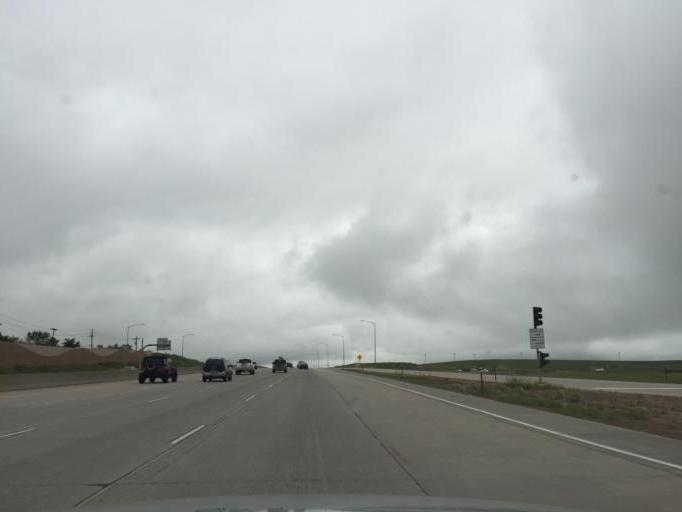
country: US
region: Colorado
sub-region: Park County
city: Castle Pines North
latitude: 39.4737
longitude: -104.8724
